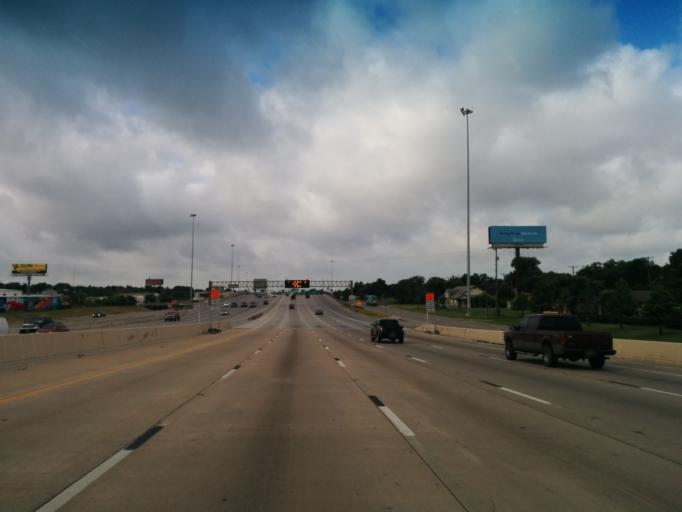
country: US
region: Texas
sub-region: Bexar County
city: Olmos Park
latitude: 29.4652
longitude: -98.5160
